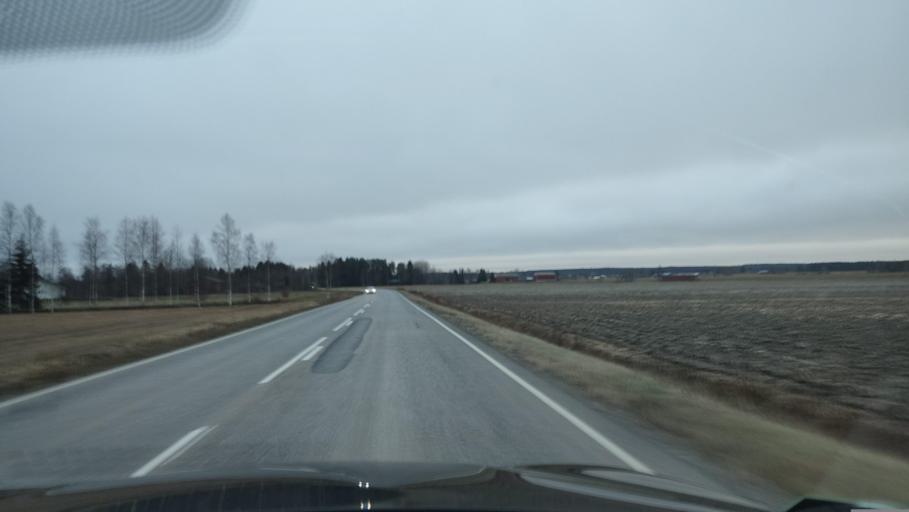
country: FI
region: Southern Ostrobothnia
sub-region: Suupohja
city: Kauhajoki
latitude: 62.3416
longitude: 21.9948
